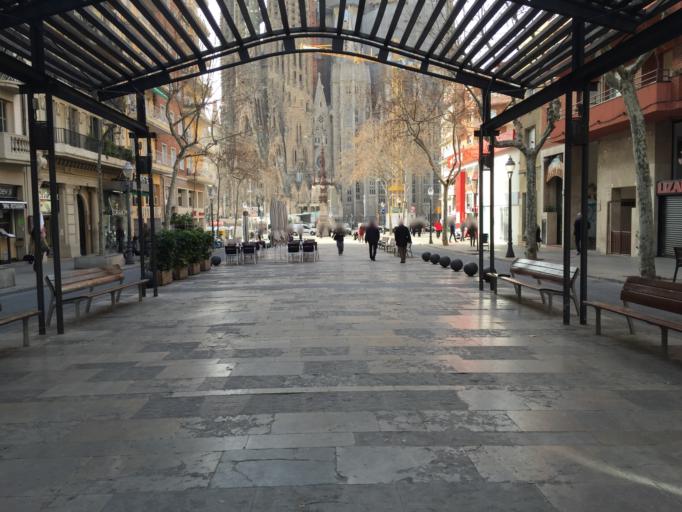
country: ES
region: Catalonia
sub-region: Provincia de Barcelona
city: Horta-Guinardo
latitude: 41.4054
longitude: 2.1744
